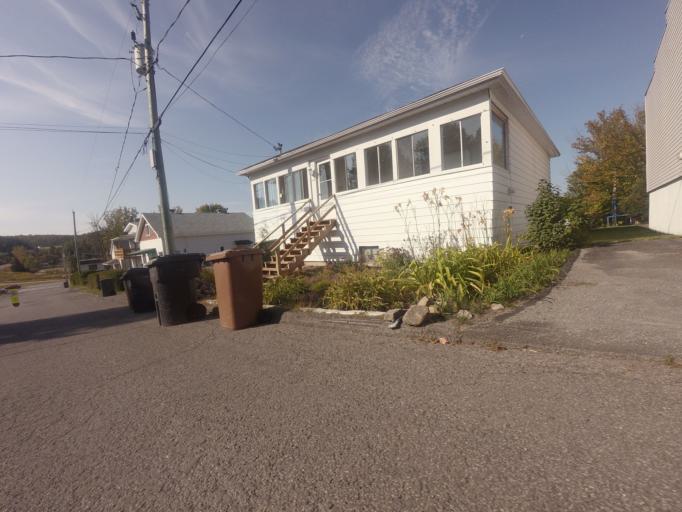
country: CA
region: Quebec
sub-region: Laurentides
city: Sainte-Agathe-des-Monts
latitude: 46.0448
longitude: -74.2684
